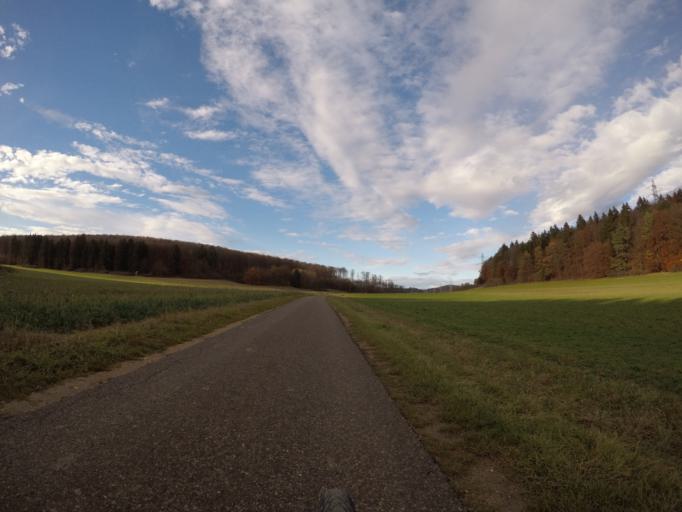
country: DE
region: Baden-Wuerttemberg
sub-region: Tuebingen Region
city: Sankt Johann
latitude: 48.4567
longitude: 9.3175
